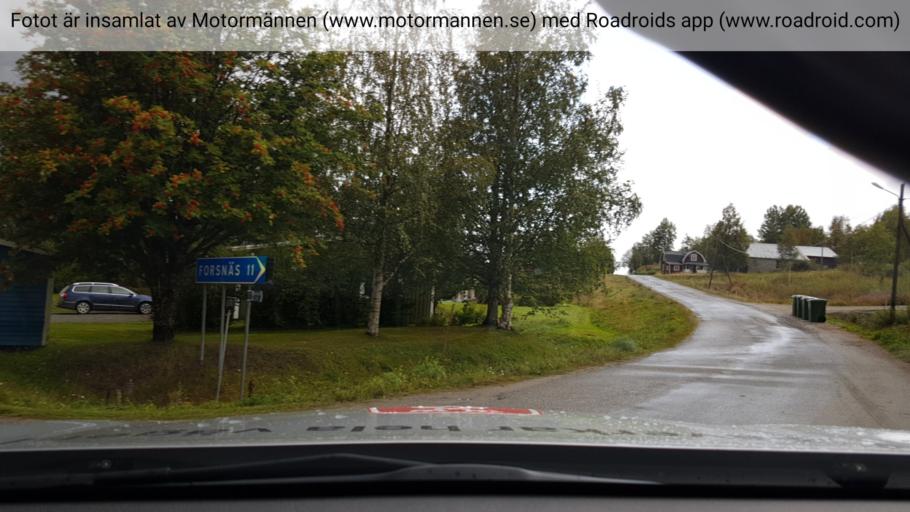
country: SE
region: Vaesterbotten
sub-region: Asele Kommun
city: Asele
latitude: 64.1866
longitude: 16.9161
